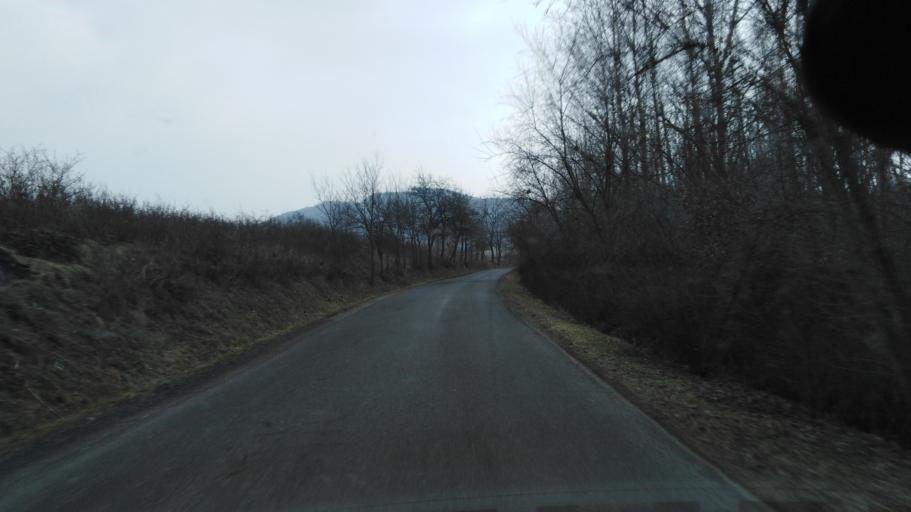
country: HU
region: Nograd
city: Tar
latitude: 48.0285
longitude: 19.7050
